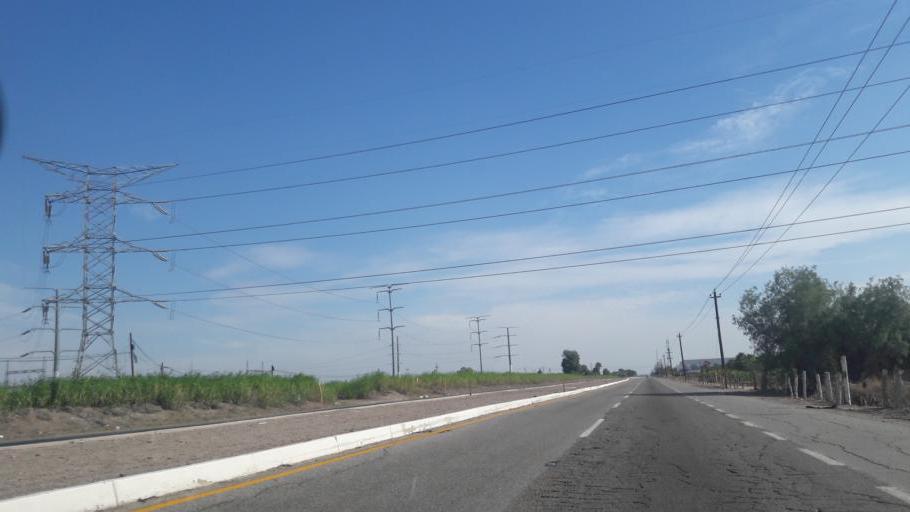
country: MX
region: Baja California
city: Progreso
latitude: 32.5958
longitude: -115.6344
